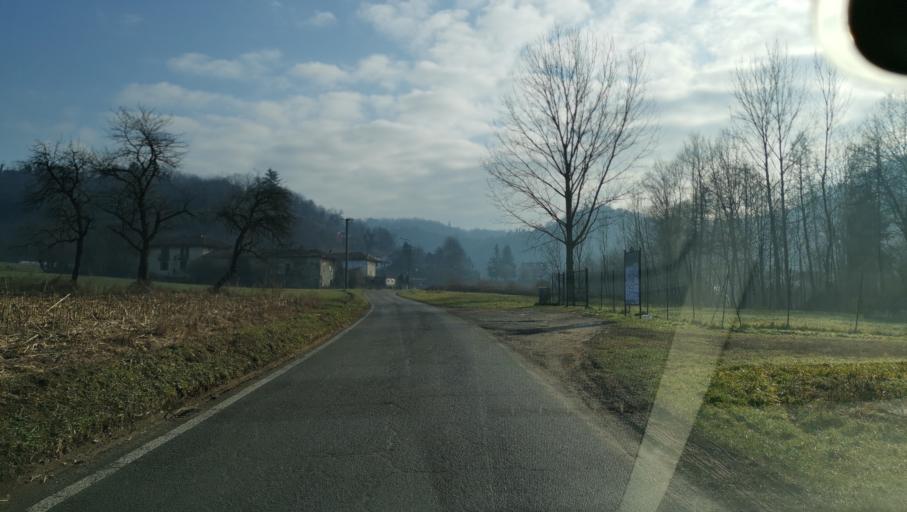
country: IT
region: Piedmont
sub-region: Provincia di Torino
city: San Raffaele Cimena
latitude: 45.1373
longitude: 7.8427
